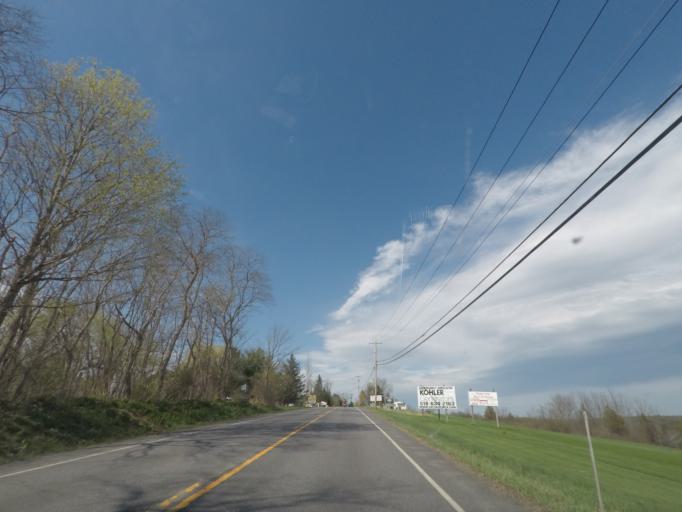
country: US
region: New York
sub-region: Greene County
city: Cairo
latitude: 42.4017
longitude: -74.0276
